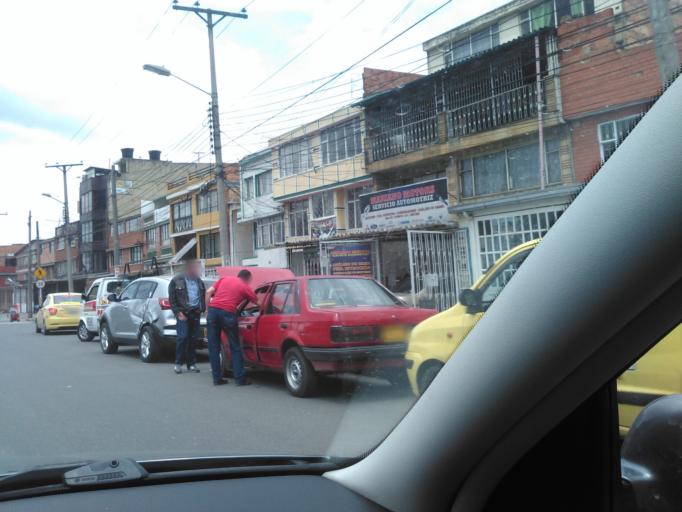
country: CO
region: Bogota D.C.
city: Bogota
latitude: 4.6181
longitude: -74.1074
